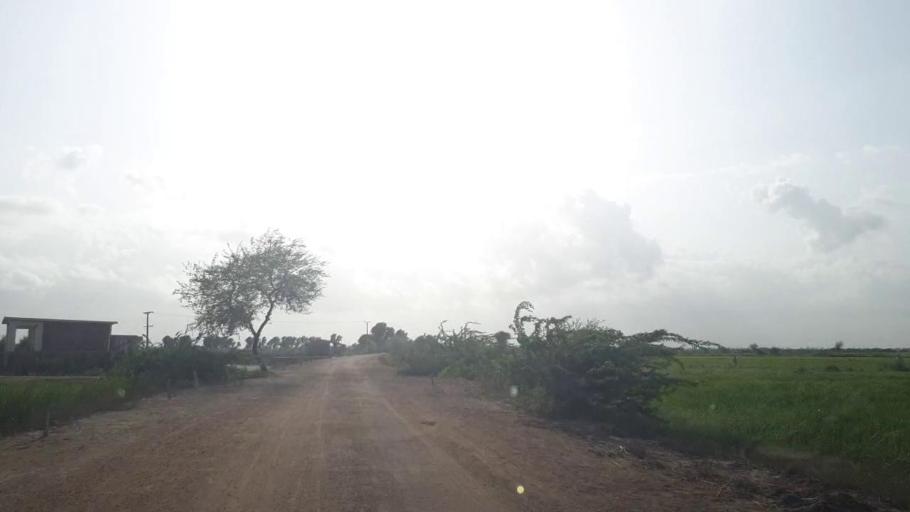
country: PK
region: Sindh
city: Kadhan
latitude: 24.6265
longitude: 69.0926
